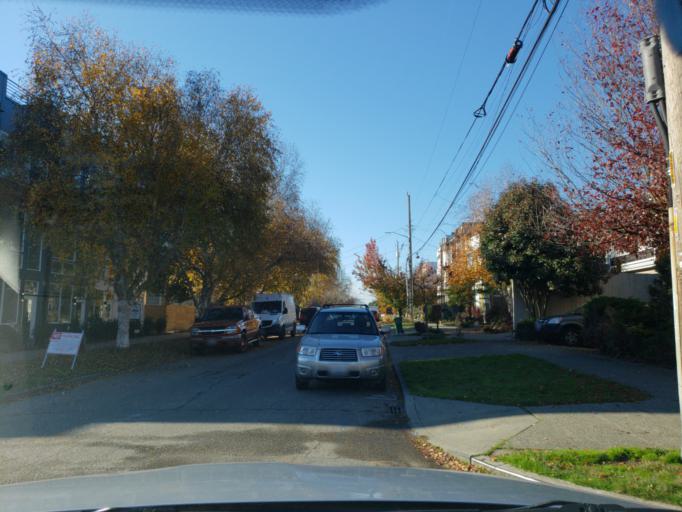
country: US
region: Washington
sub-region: King County
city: Seattle
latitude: 47.6746
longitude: -122.3848
